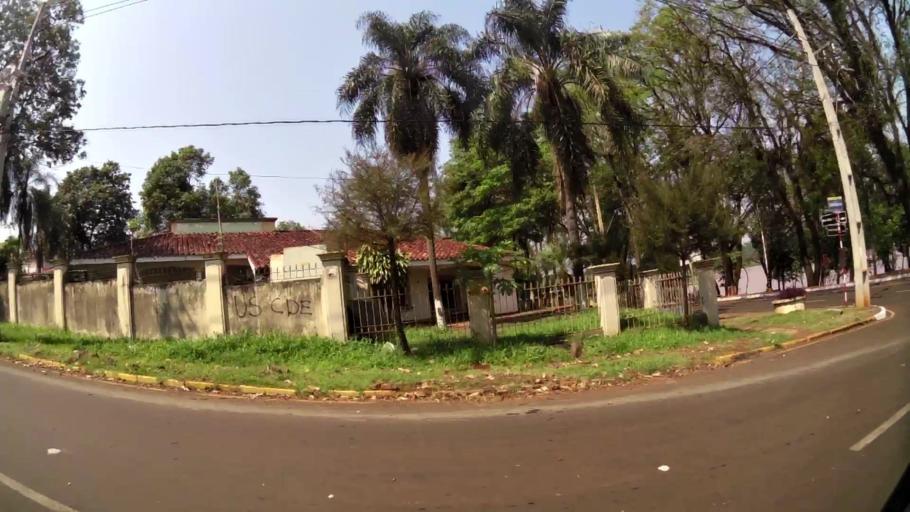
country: PY
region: Alto Parana
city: Ciudad del Este
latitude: -25.5157
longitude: -54.6181
